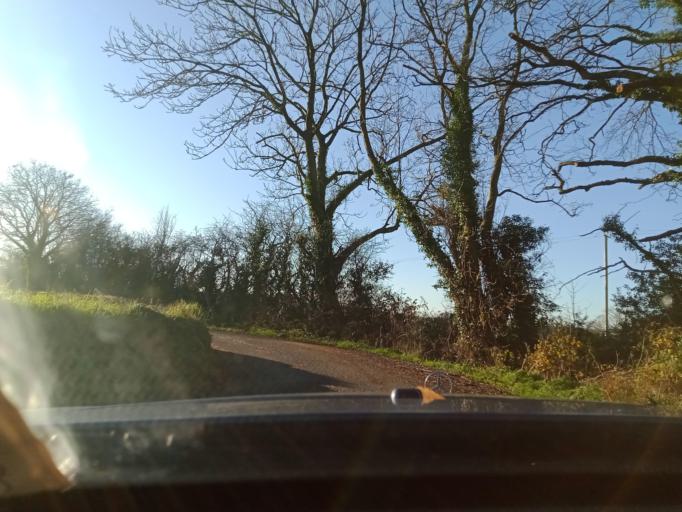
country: IE
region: Munster
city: Carrick-on-Suir
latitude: 52.4389
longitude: -7.4172
